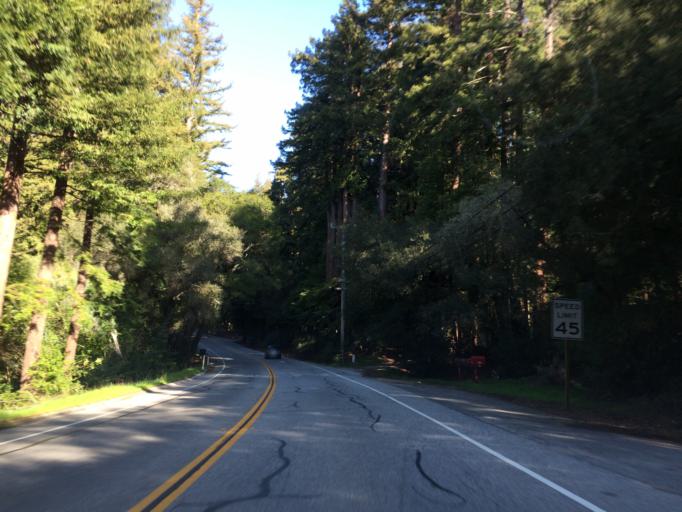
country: US
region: California
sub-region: Santa Cruz County
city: Boulder Creek
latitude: 37.1444
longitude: -122.1321
